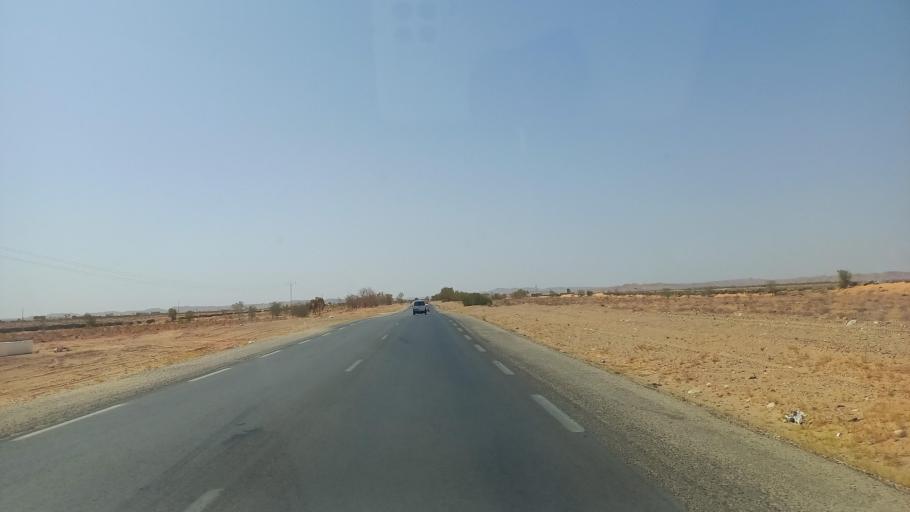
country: TN
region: Madanin
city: Medenine
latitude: 33.2182
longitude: 10.4487
